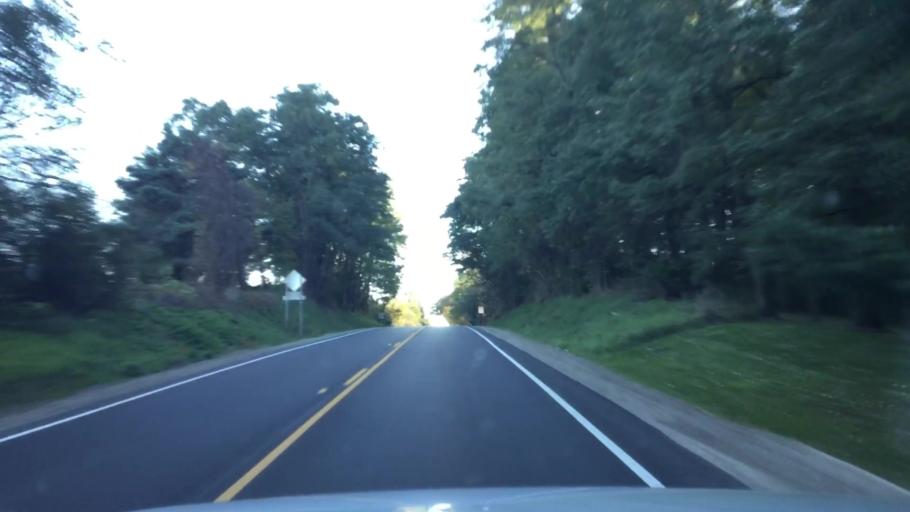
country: US
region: Michigan
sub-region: Lapeer County
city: Almont
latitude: 42.9154
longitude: -83.1433
